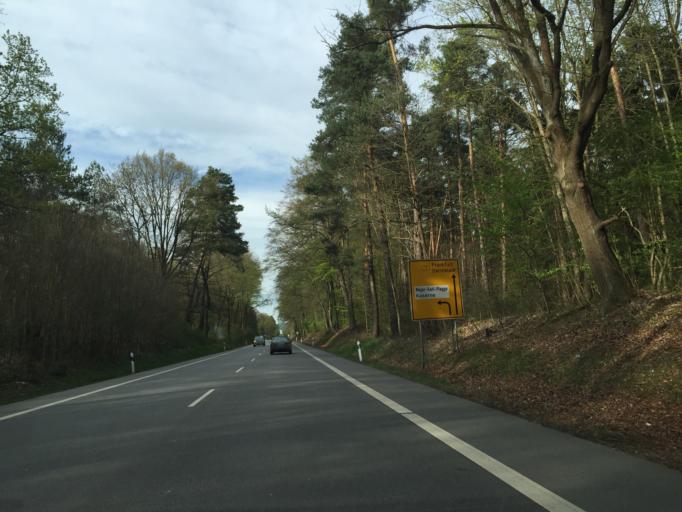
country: DE
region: Hesse
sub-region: Regierungsbezirk Darmstadt
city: Seeheim-Jugenheim
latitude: 49.7910
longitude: 8.6344
